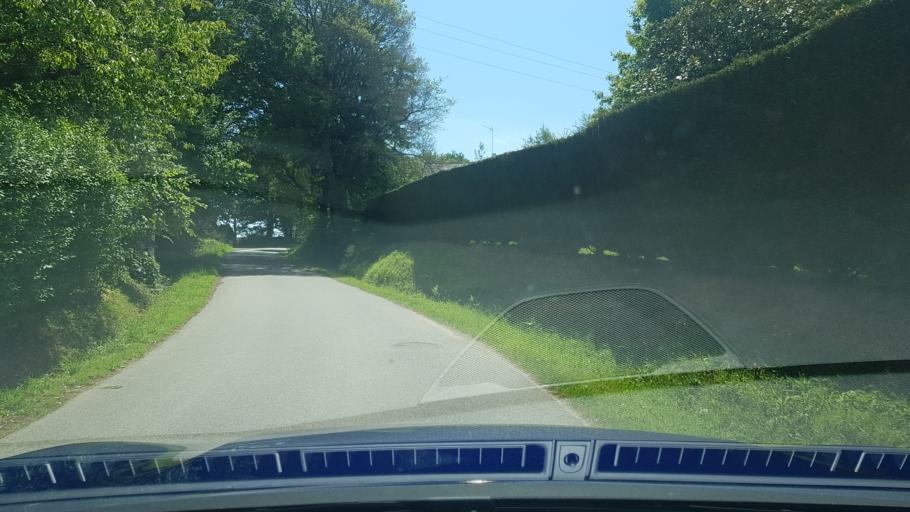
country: FR
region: Brittany
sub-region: Departement du Morbihan
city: Pont-Scorff
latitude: 47.8211
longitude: -3.4126
